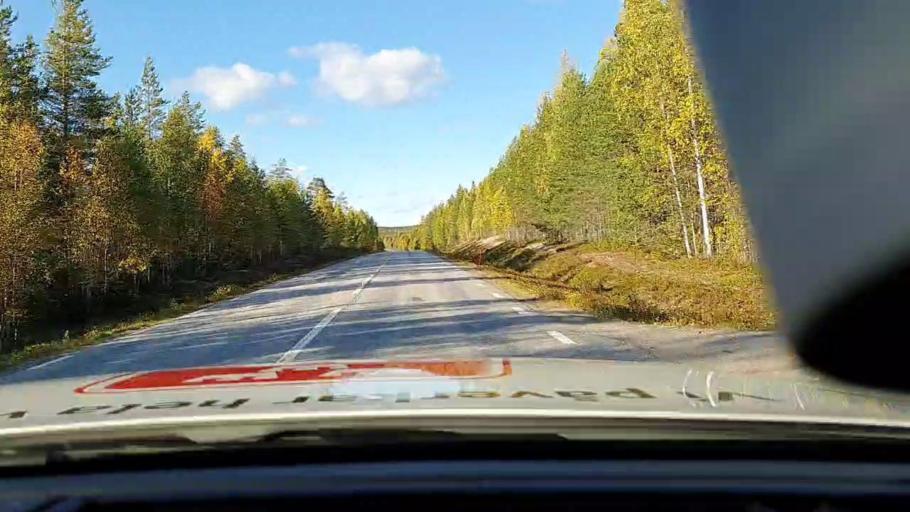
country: SE
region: Norrbotten
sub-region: Pitea Kommun
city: Norrfjarden
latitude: 65.4549
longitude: 21.4558
